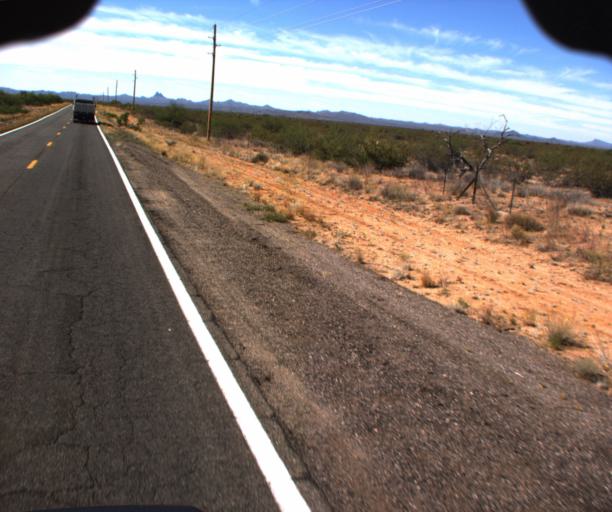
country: US
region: Arizona
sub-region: Yavapai County
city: Congress
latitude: 34.0988
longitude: -112.8297
